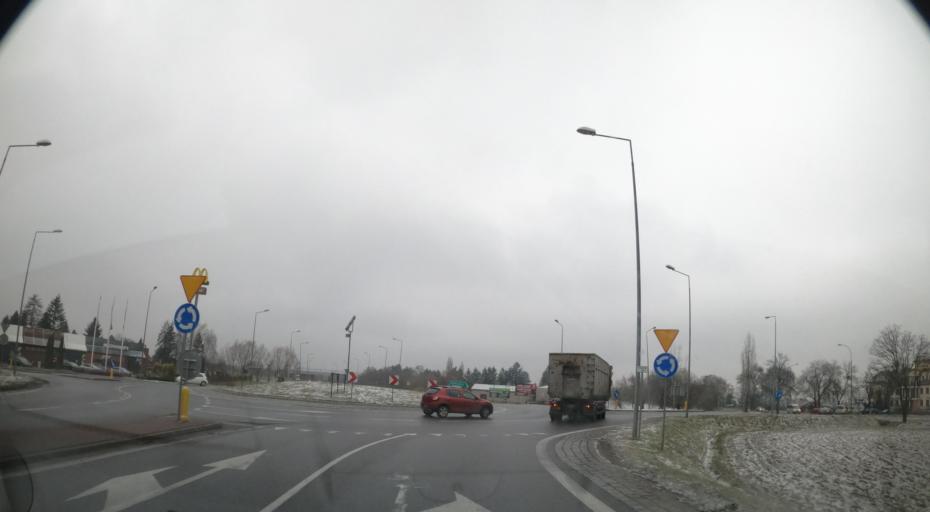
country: PL
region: Masovian Voivodeship
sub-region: Powiat sochaczewski
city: Sochaczew
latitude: 52.2262
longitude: 20.2665
